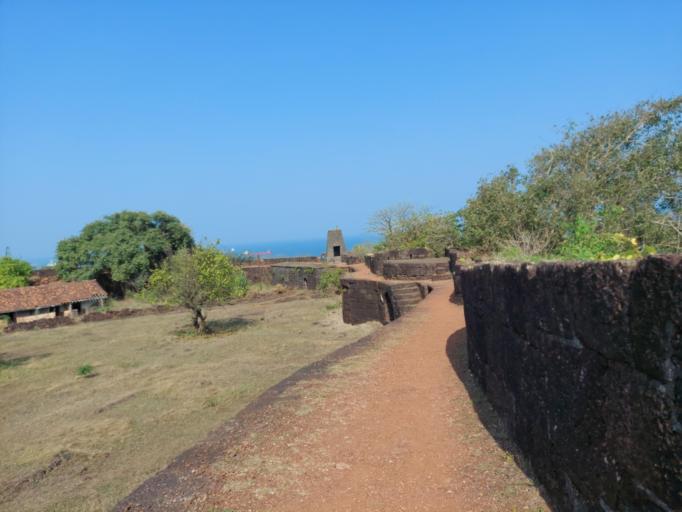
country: IN
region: Maharashtra
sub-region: Ratnagiri
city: Guhagar
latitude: 17.3012
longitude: 73.2218
